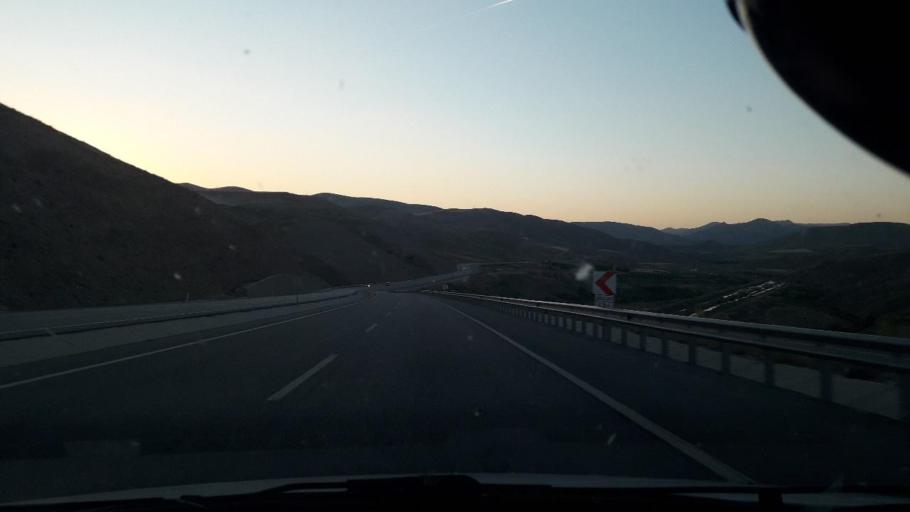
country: TR
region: Malatya
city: Yazihan
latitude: 38.6217
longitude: 38.1681
